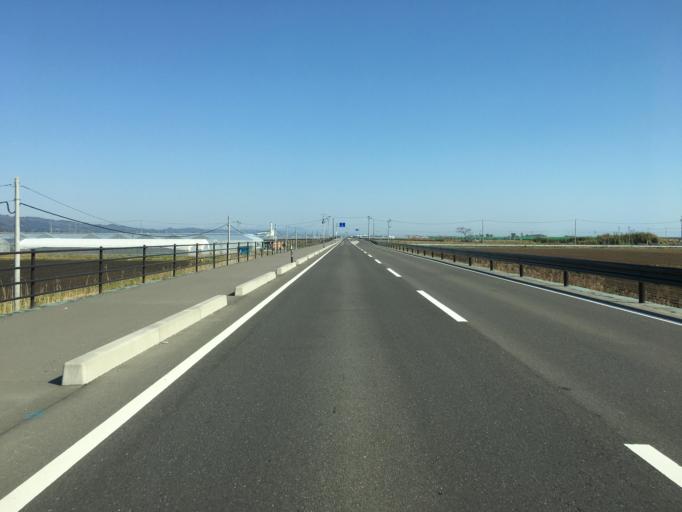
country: JP
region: Miyagi
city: Watari
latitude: 37.9399
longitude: 140.9092
